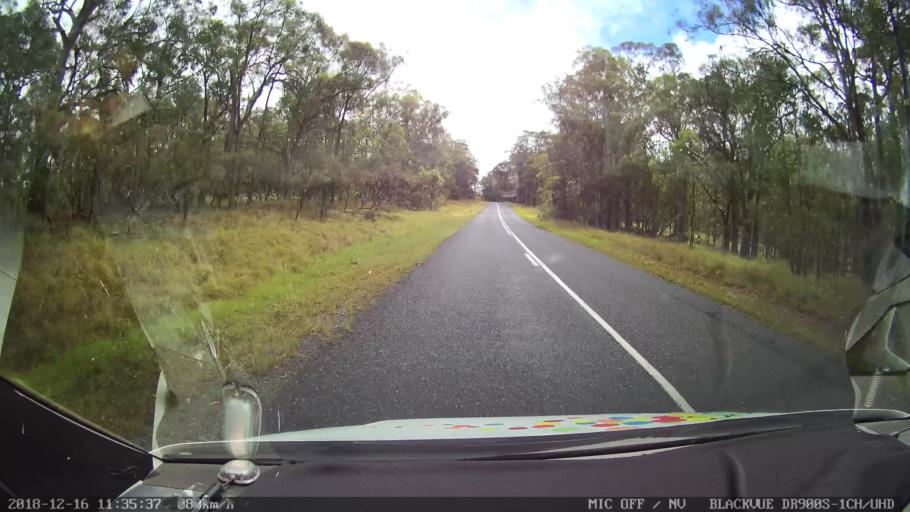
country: AU
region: New South Wales
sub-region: Tenterfield Municipality
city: Carrolls Creek
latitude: -28.9882
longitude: 152.1639
